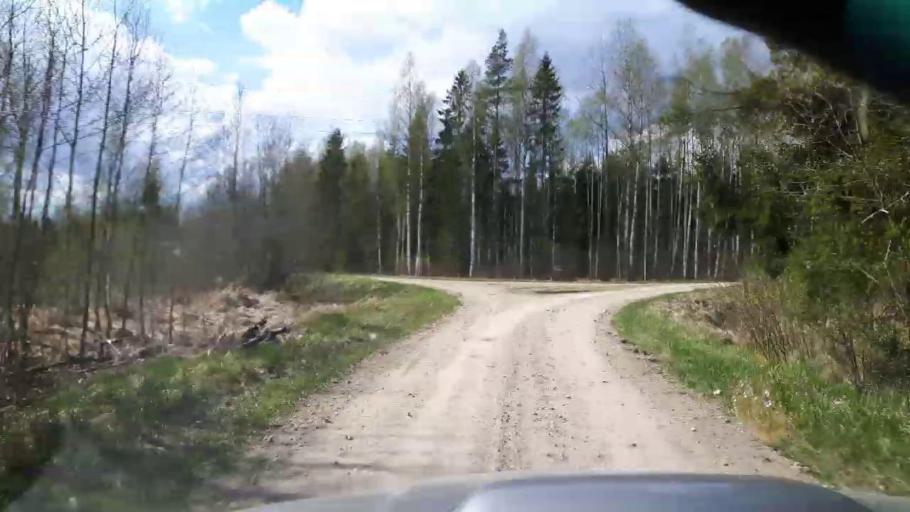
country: EE
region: Paernumaa
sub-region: Tootsi vald
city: Tootsi
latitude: 58.4431
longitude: 24.9218
